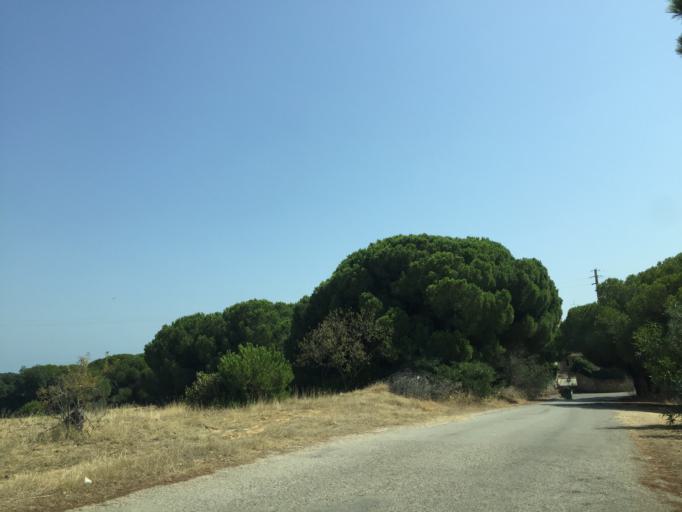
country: PT
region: Faro
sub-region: Albufeira
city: Ferreiras
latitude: 37.1044
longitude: -8.2014
